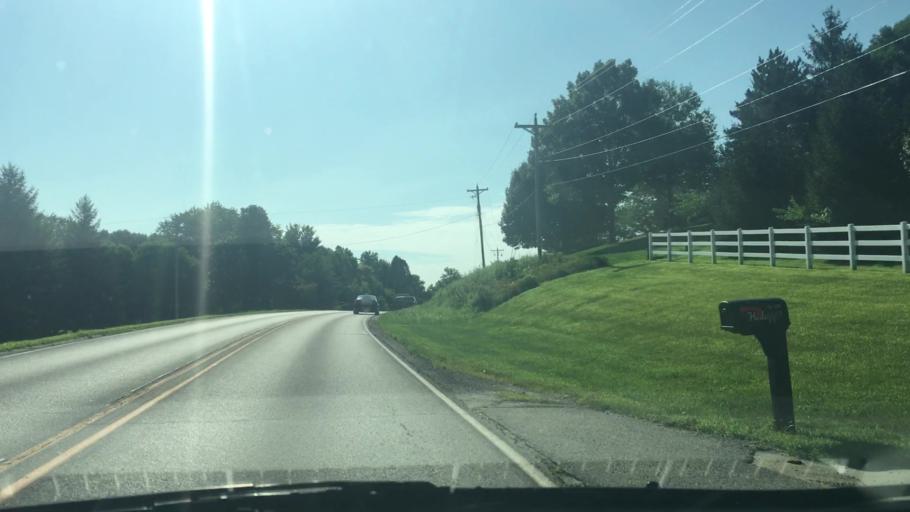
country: US
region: Iowa
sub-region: Johnson County
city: North Liberty
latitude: 41.7214
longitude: -91.5587
